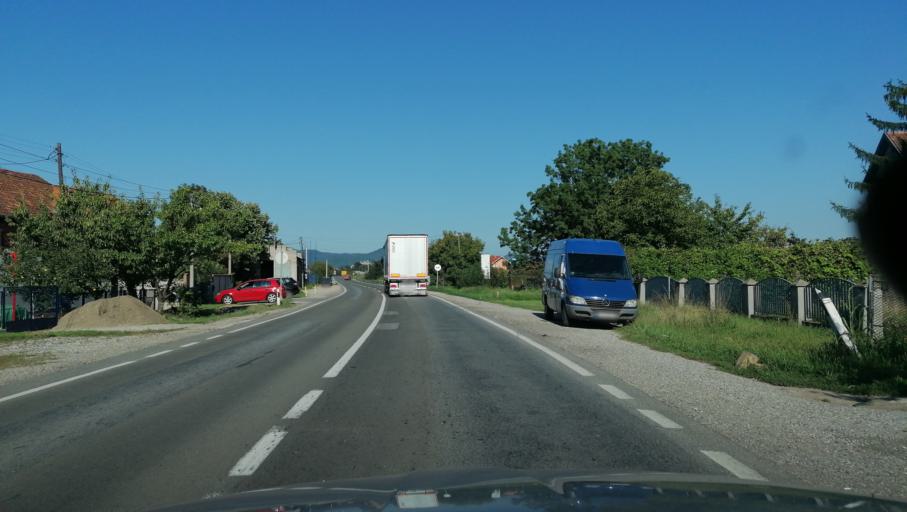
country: RS
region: Central Serbia
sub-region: Raski Okrug
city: Kraljevo
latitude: 43.7317
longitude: 20.6597
